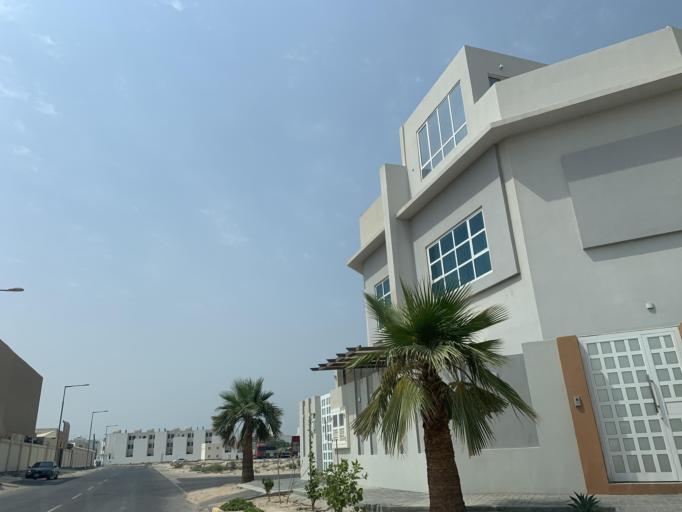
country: BH
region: Manama
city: Jidd Hafs
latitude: 26.2084
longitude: 50.4866
